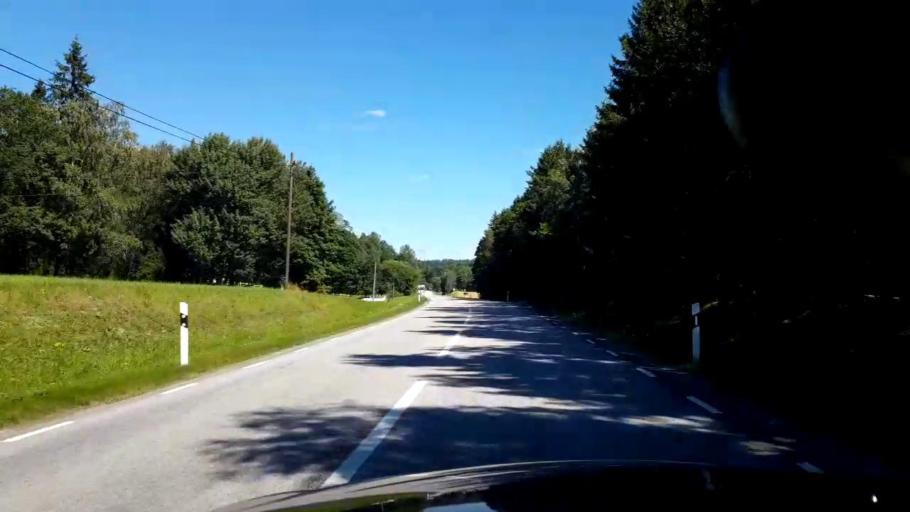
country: SE
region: Uppsala
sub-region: Habo Kommun
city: Balsta
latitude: 59.6342
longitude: 17.6044
